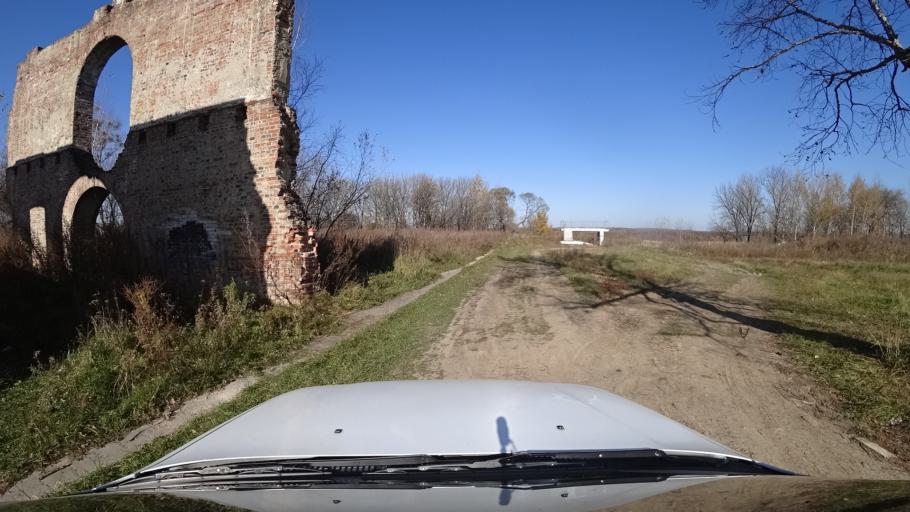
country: RU
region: Primorskiy
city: Dal'nerechensk
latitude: 45.9459
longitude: 133.6864
